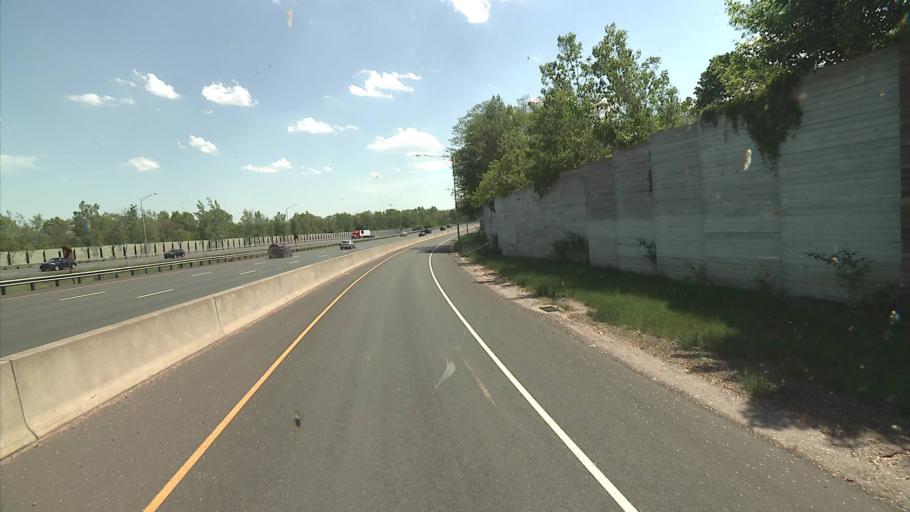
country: US
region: Connecticut
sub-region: New Haven County
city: Cheshire Village
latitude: 41.5850
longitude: -72.8993
